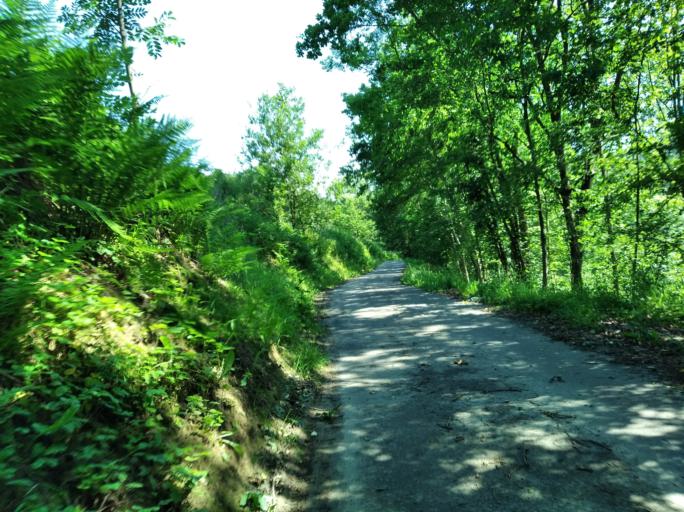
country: PL
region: Subcarpathian Voivodeship
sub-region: Powiat strzyzowski
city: Jawornik
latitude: 49.8227
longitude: 21.8432
